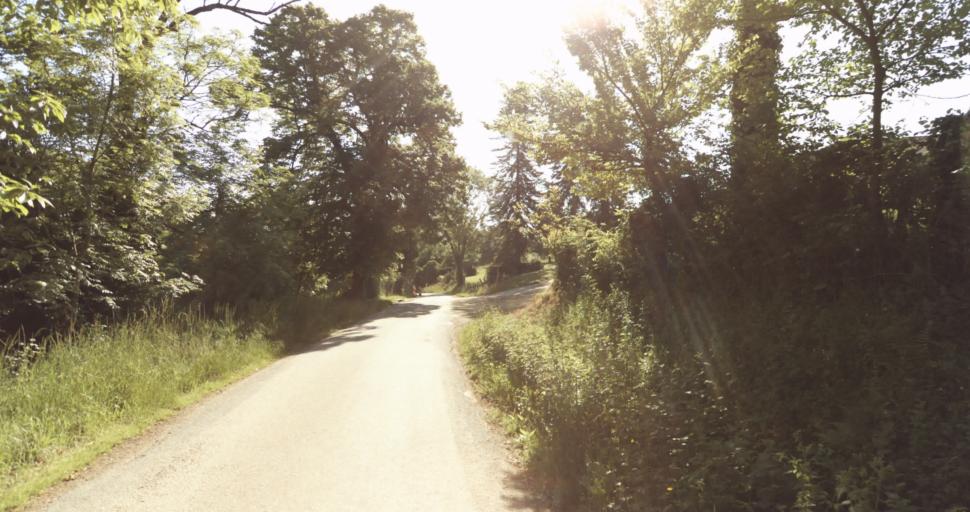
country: FR
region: Limousin
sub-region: Departement de la Haute-Vienne
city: Bosmie-l'Aiguille
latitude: 45.7214
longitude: 1.2333
